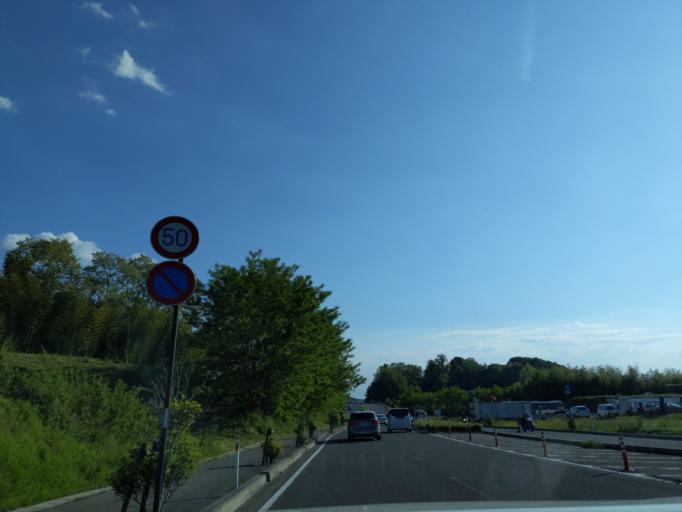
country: JP
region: Fukushima
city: Sukagawa
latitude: 37.2795
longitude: 140.3798
